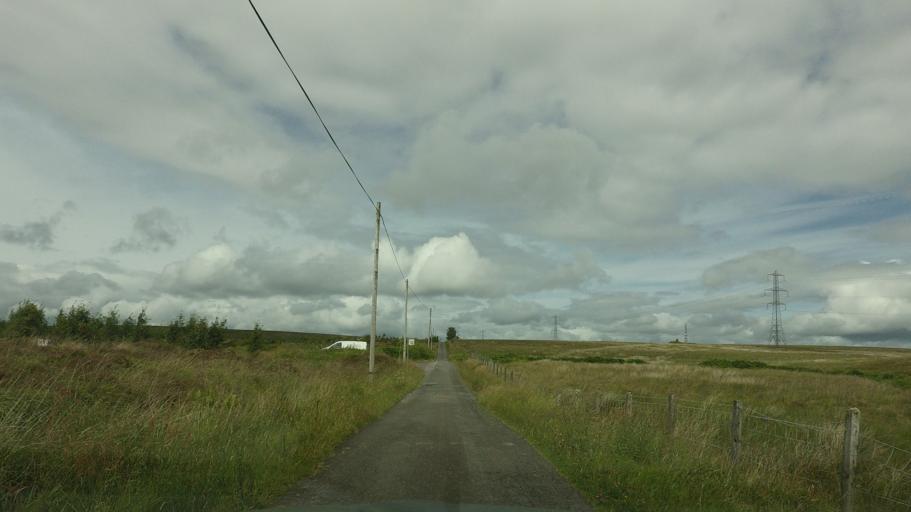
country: GB
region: Scotland
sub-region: Stirling
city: Killearn
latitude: 56.0923
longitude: -4.4322
